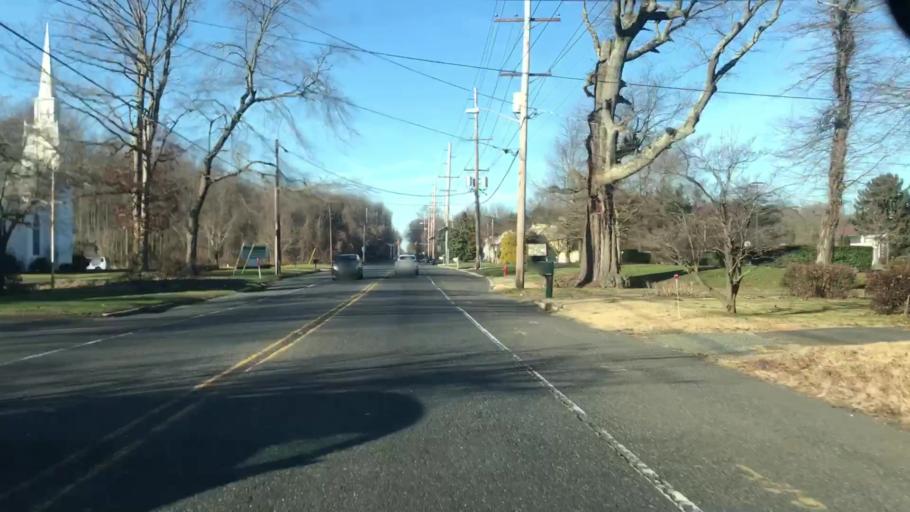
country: US
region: New Jersey
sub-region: Burlington County
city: Burlington
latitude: 40.0505
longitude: -74.8474
